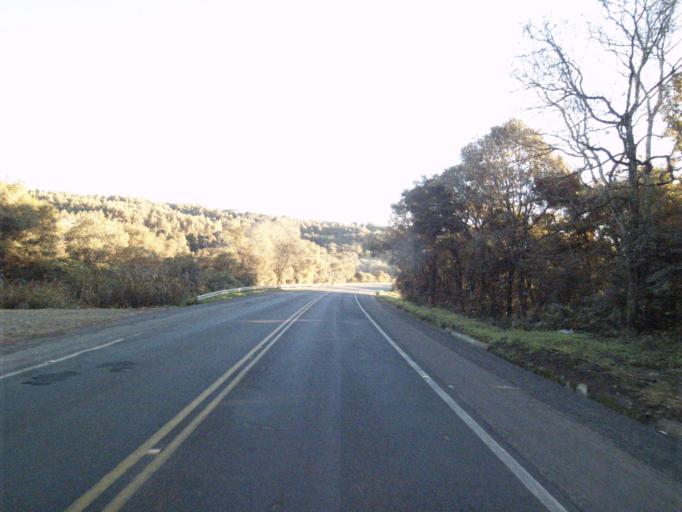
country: BR
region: Santa Catarina
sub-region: Chapeco
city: Chapeco
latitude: -26.8325
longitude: -53.0298
